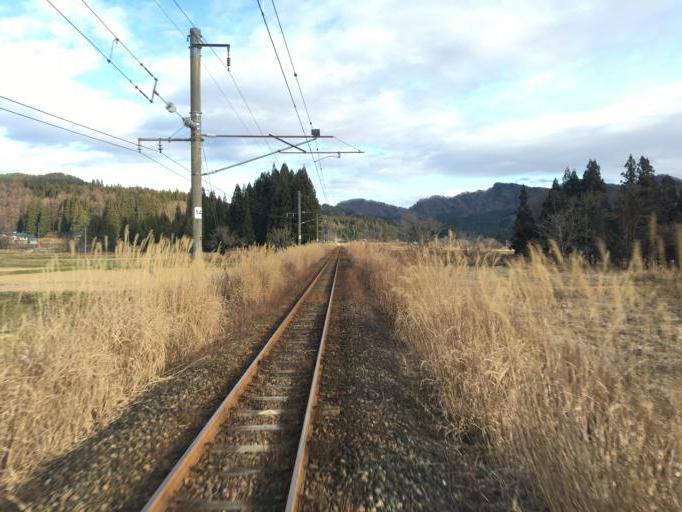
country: JP
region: Yamagata
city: Shinjo
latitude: 38.9739
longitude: 140.3272
